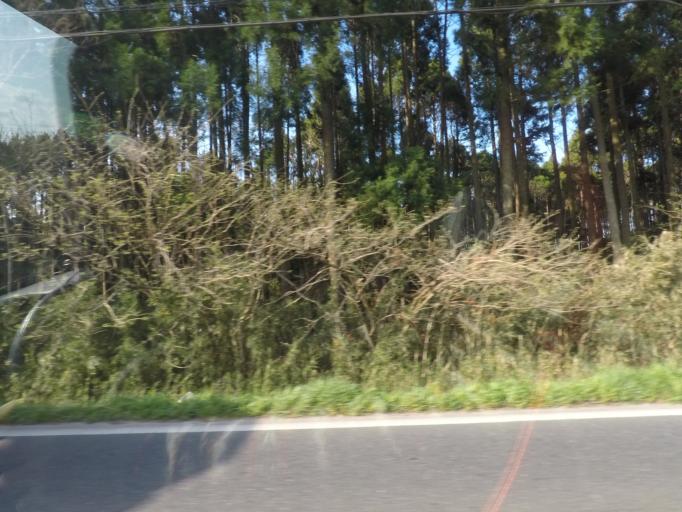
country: JP
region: Chiba
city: Yachimata
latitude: 35.6229
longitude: 140.2466
